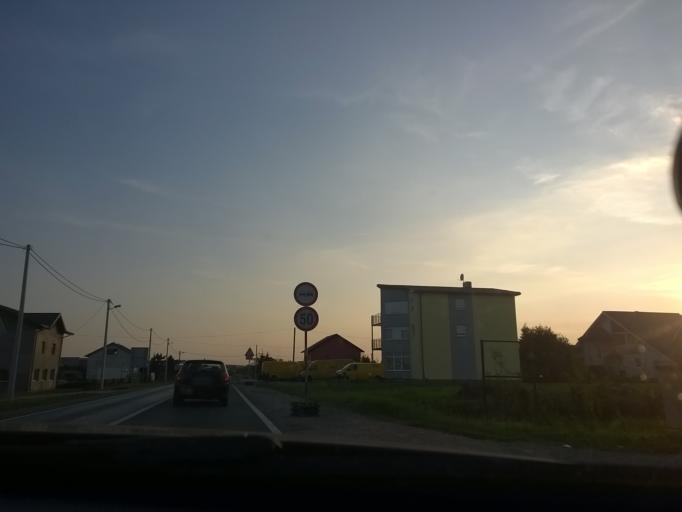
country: HR
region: Grad Zagreb
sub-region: Sesvete
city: Sesvete
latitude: 45.8630
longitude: 16.1528
